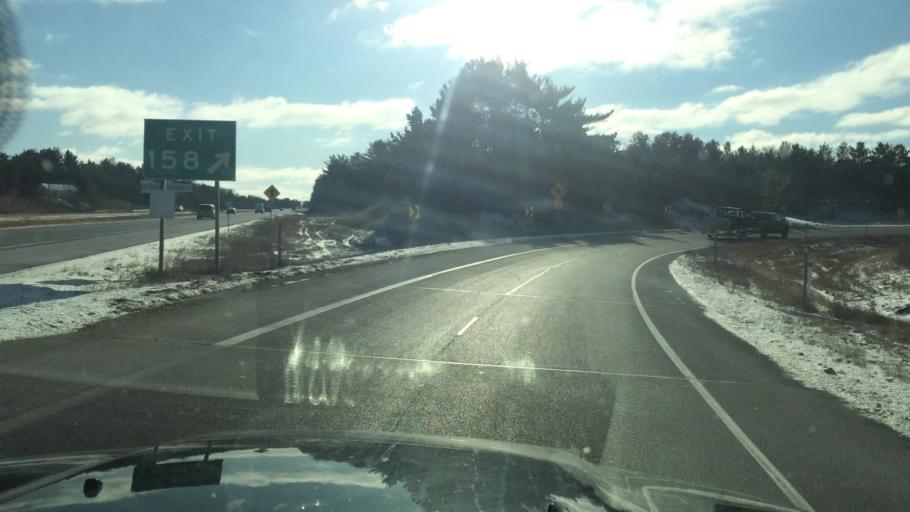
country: US
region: Wisconsin
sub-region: Portage County
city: Whiting
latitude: 44.5224
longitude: -89.5269
